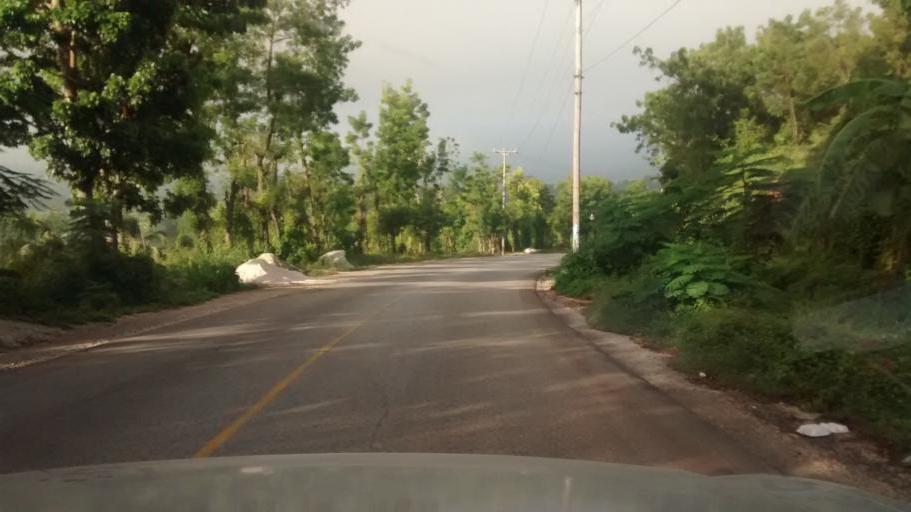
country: HT
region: Nippes
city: Miragoane
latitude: 18.3742
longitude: -73.1239
